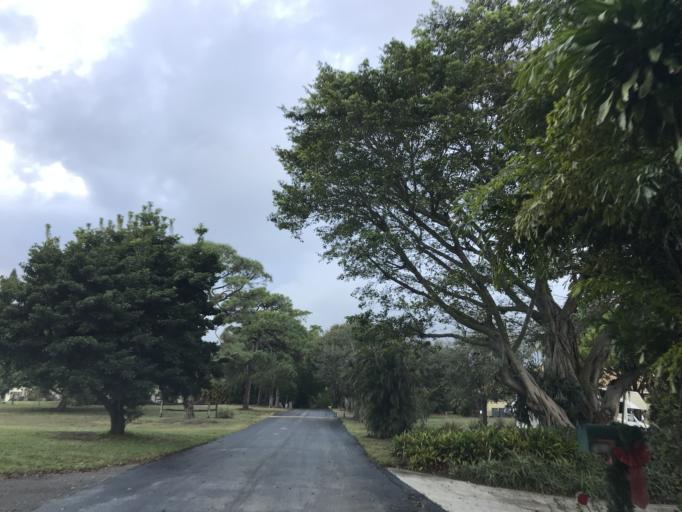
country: US
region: Florida
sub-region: Palm Beach County
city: Hypoluxo
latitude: 26.5653
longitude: -80.0718
